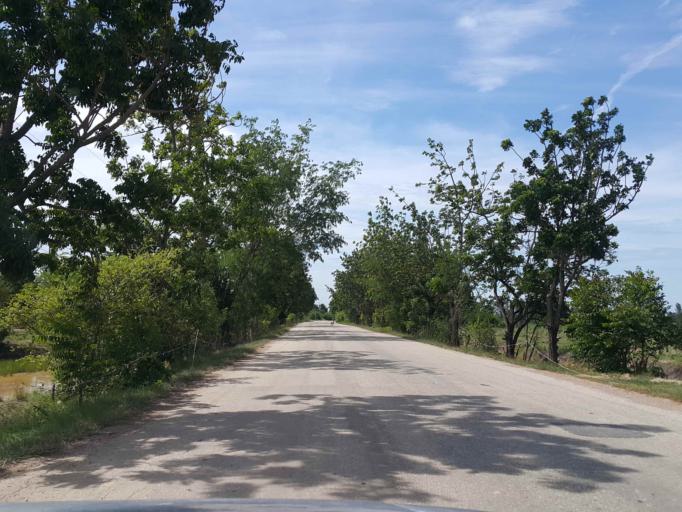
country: TH
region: Sukhothai
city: Ban Dan Lan Hoi
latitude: 17.1463
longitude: 99.5222
